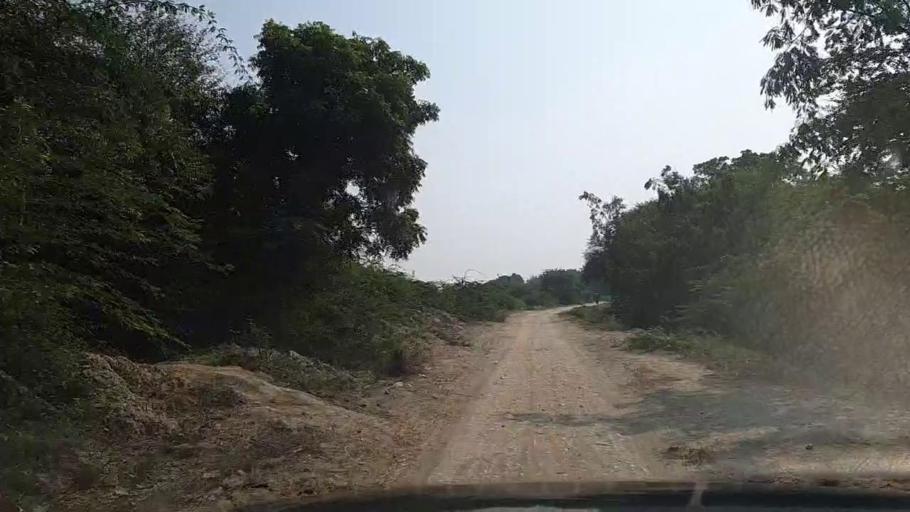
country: PK
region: Sindh
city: Mirpur Batoro
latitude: 24.7013
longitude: 68.2179
